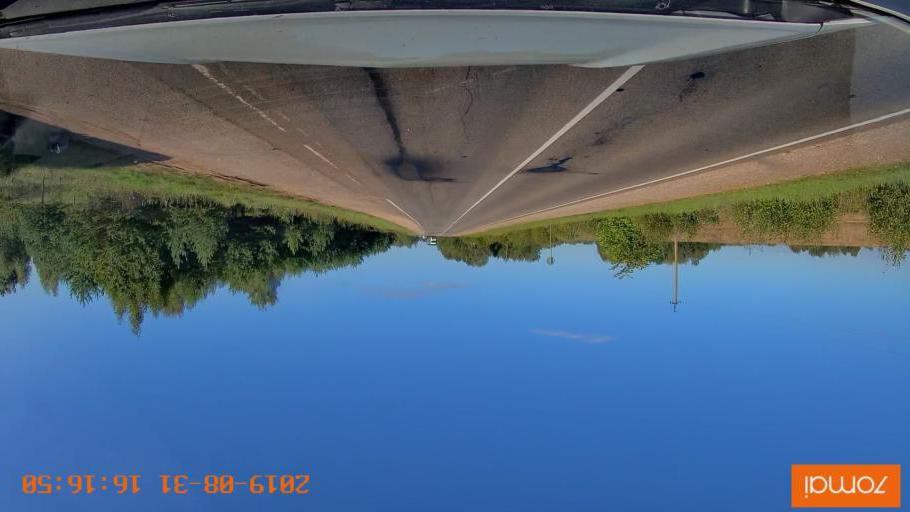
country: RU
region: Kaluga
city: Nikola-Lenivets
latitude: 54.5506
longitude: 35.5203
